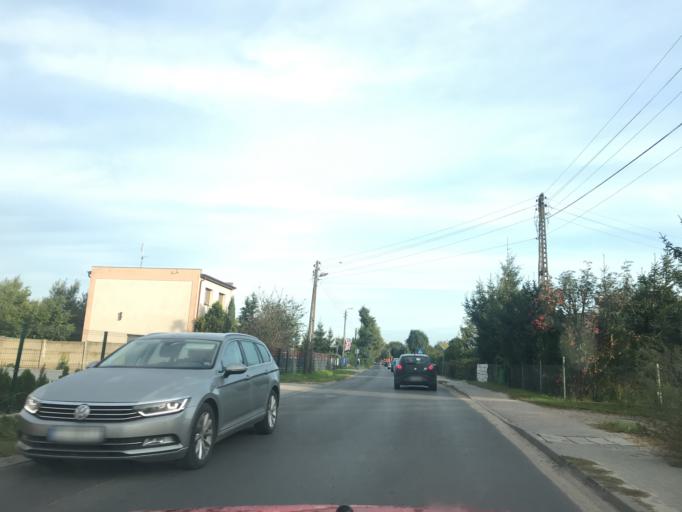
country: PL
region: Greater Poland Voivodeship
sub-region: Powiat poznanski
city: Plewiska
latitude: 52.3885
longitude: 16.7959
